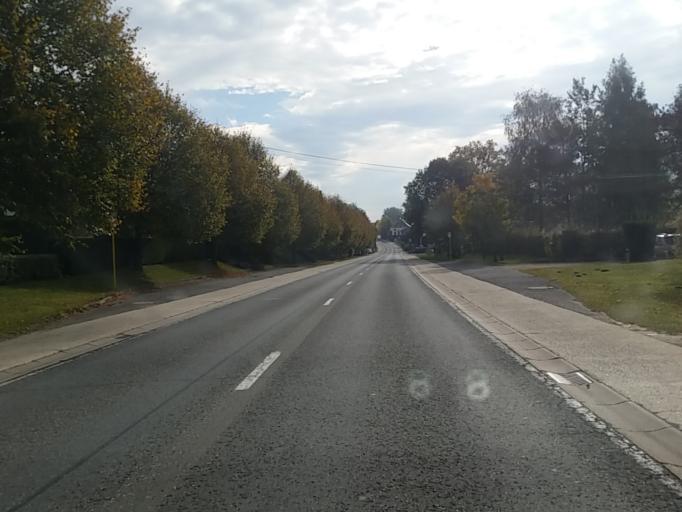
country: BE
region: Wallonia
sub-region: Province du Luxembourg
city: Tintigny
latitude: 49.6769
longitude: 5.5422
